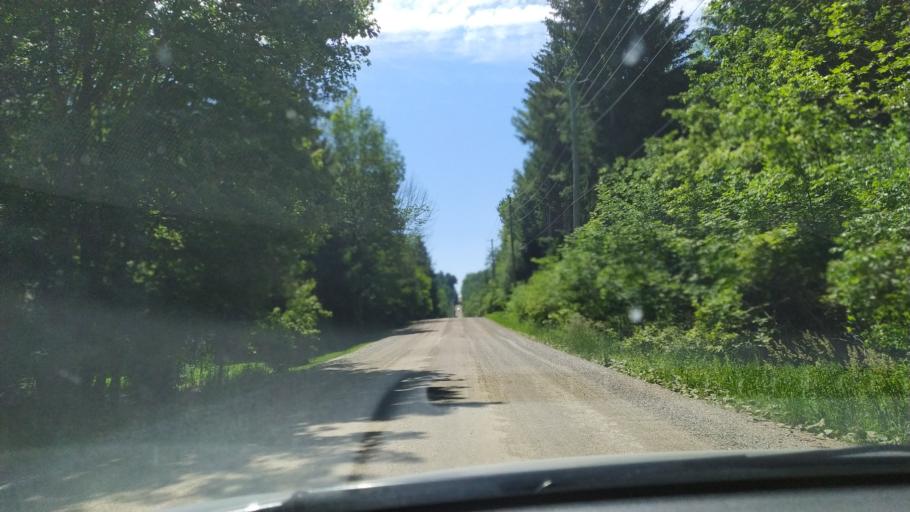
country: CA
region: Ontario
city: Waterloo
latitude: 43.4687
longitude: -80.6138
